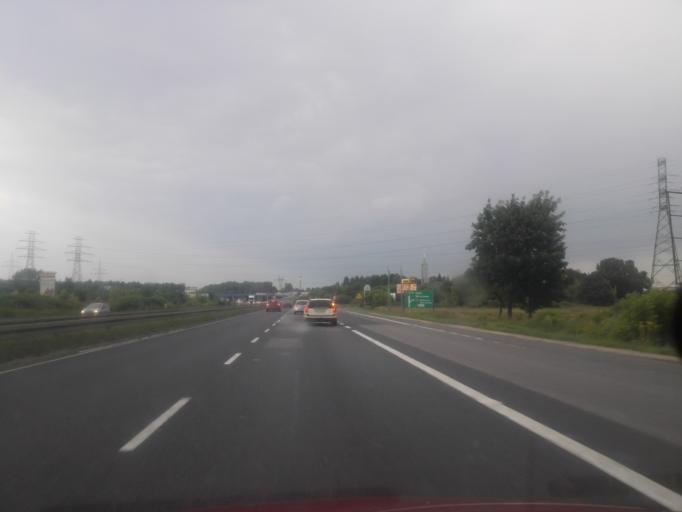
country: PL
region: Silesian Voivodeship
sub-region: Czestochowa
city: Czestochowa
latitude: 50.8263
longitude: 19.1435
